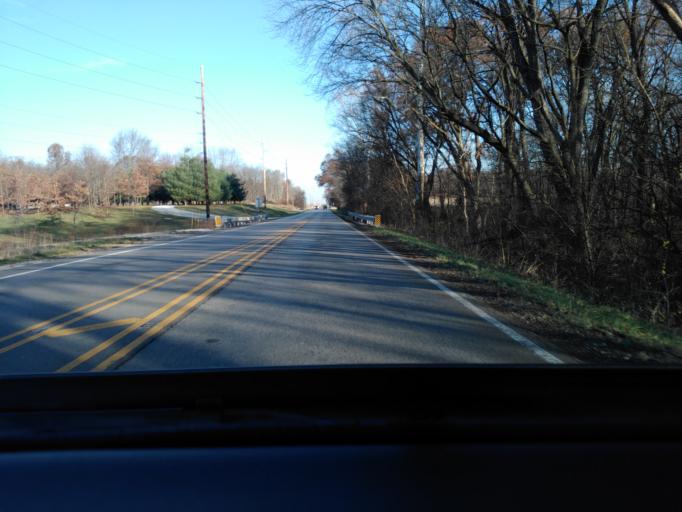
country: US
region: Illinois
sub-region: Madison County
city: Saint Jacob
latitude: 38.7210
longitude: -89.8011
